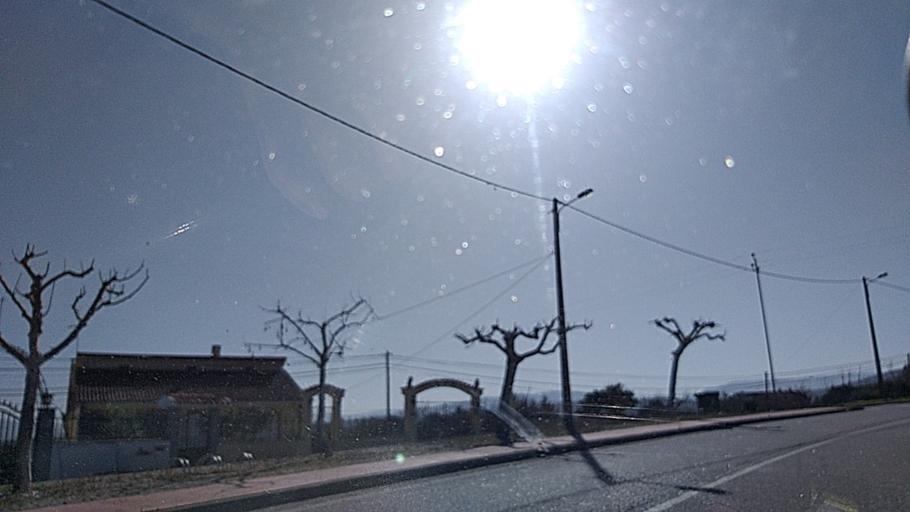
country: PT
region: Guarda
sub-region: Celorico da Beira
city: Celorico da Beira
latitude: 40.6503
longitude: -7.3824
